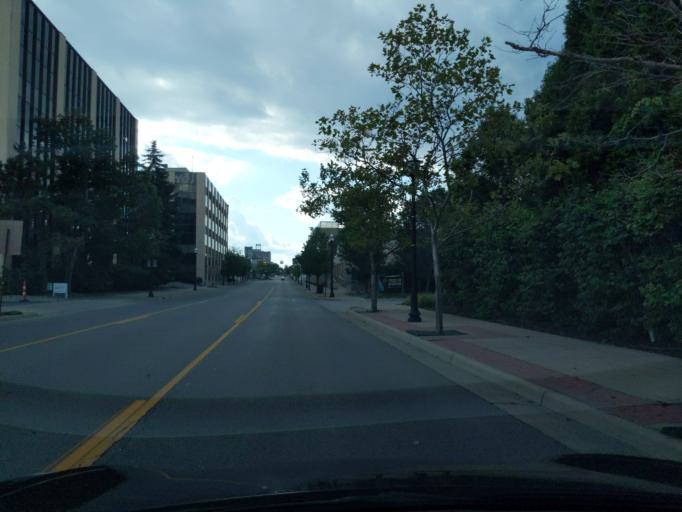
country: US
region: Michigan
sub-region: Jackson County
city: Jackson
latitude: 42.2457
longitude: -84.4018
